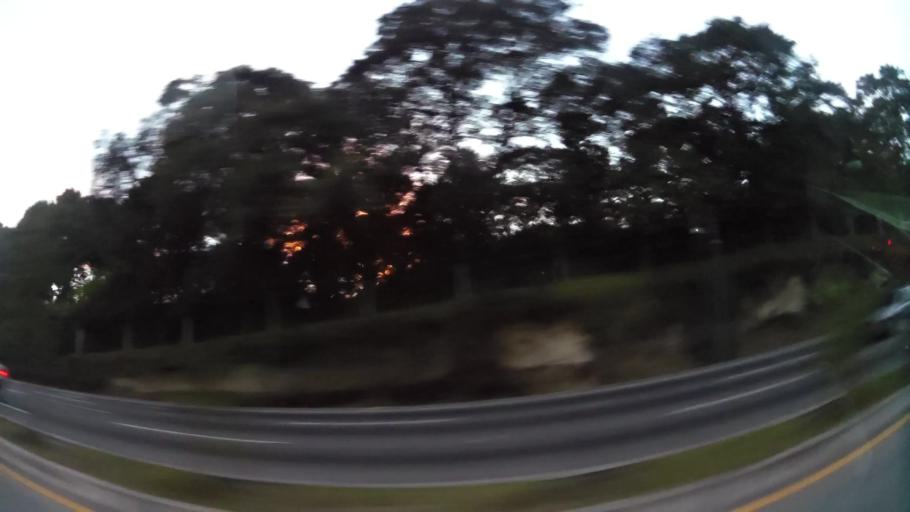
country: GT
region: Guatemala
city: Mixco
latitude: 14.6173
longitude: -90.6171
